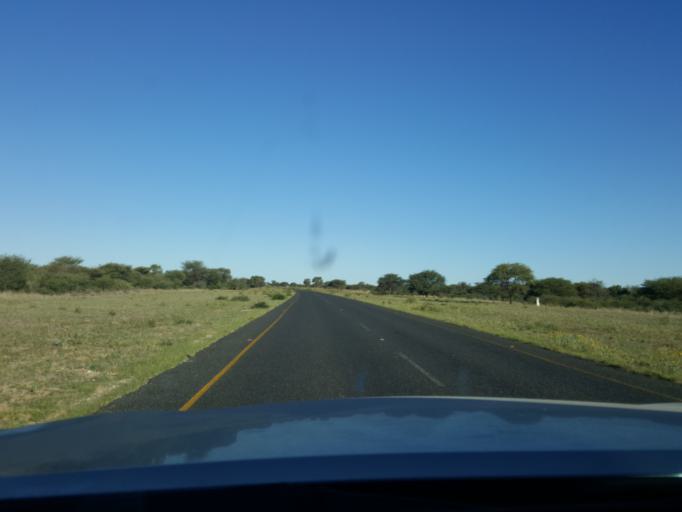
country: BW
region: Southern
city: Khakhea
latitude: -24.2183
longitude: 23.2296
